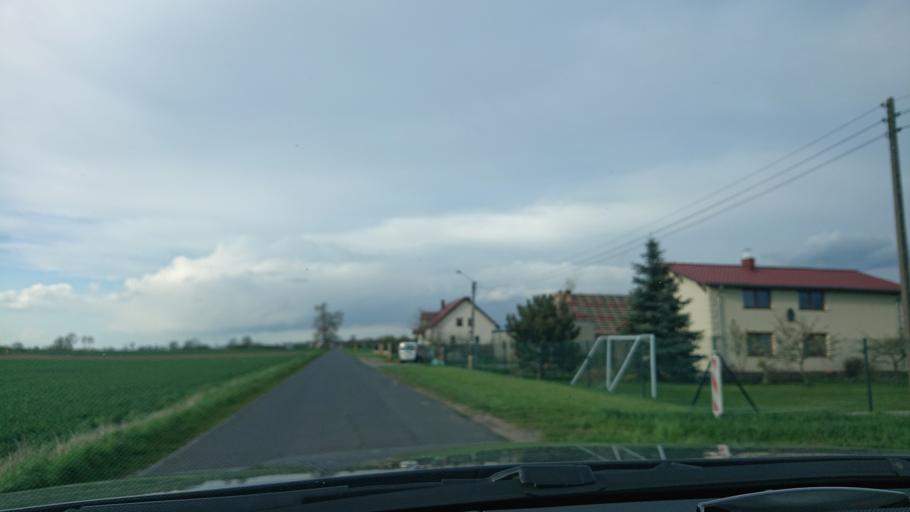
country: PL
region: Greater Poland Voivodeship
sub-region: Powiat gnieznienski
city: Klecko
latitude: 52.5822
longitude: 17.4822
